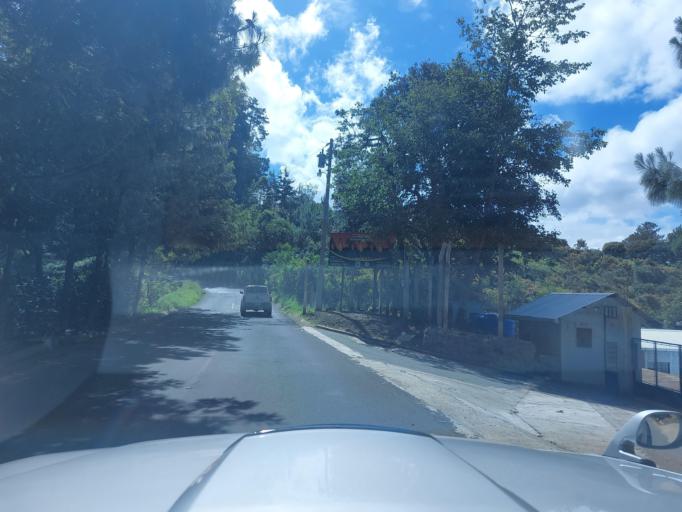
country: GT
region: Chimaltenango
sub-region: Municipio de San Juan Comalapa
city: Comalapa
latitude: 14.7109
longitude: -90.8923
